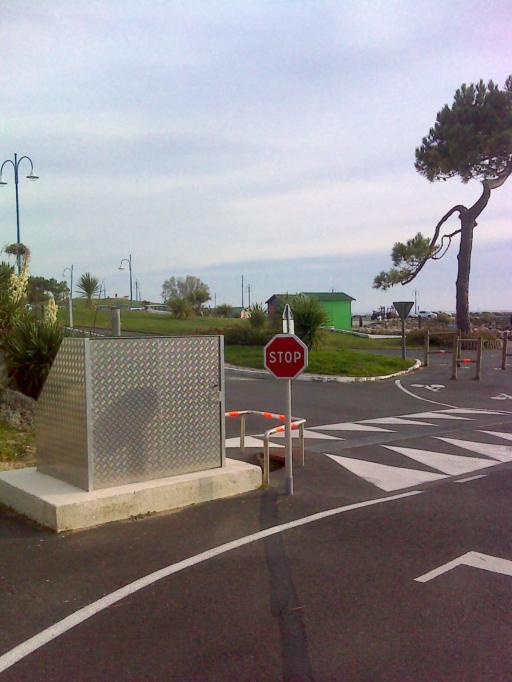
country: FR
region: Poitou-Charentes
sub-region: Departement de la Charente-Maritime
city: Les Mathes
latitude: 45.6846
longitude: -1.1822
